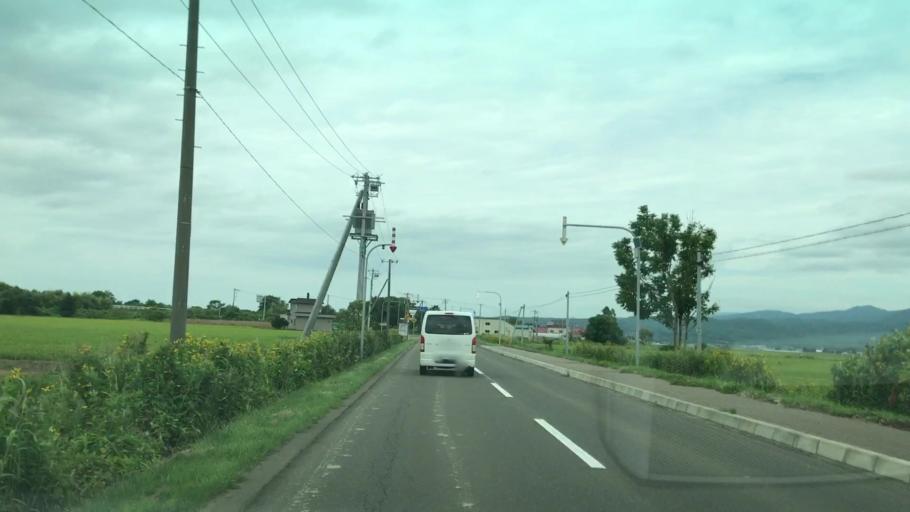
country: JP
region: Hokkaido
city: Iwanai
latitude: 43.0012
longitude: 140.5878
